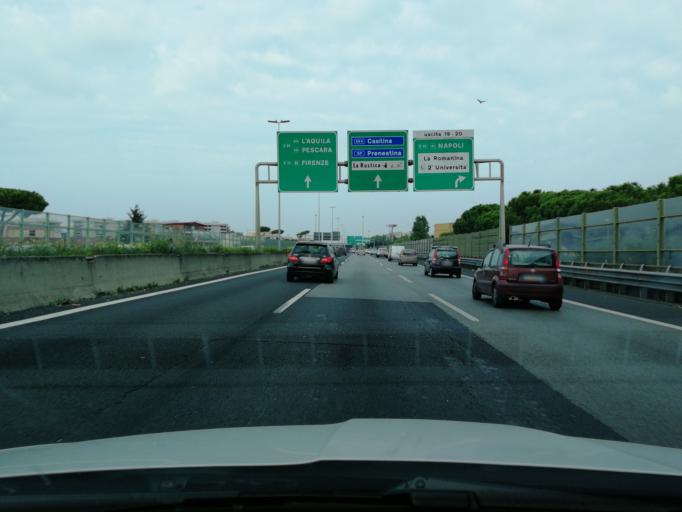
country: IT
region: Latium
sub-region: Citta metropolitana di Roma Capitale
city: Ciampino
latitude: 41.8436
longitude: 12.5937
